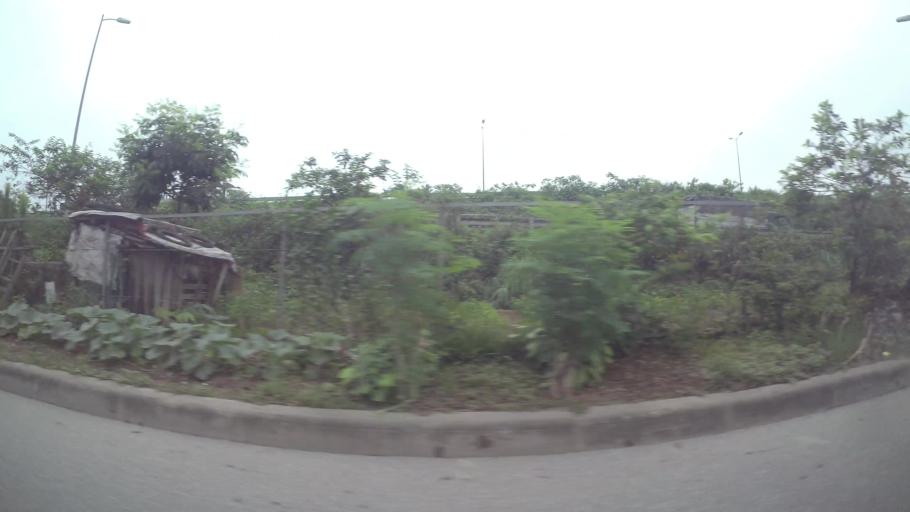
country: VN
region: Ha Noi
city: Hai BaTrung
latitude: 20.9807
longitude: 105.8896
